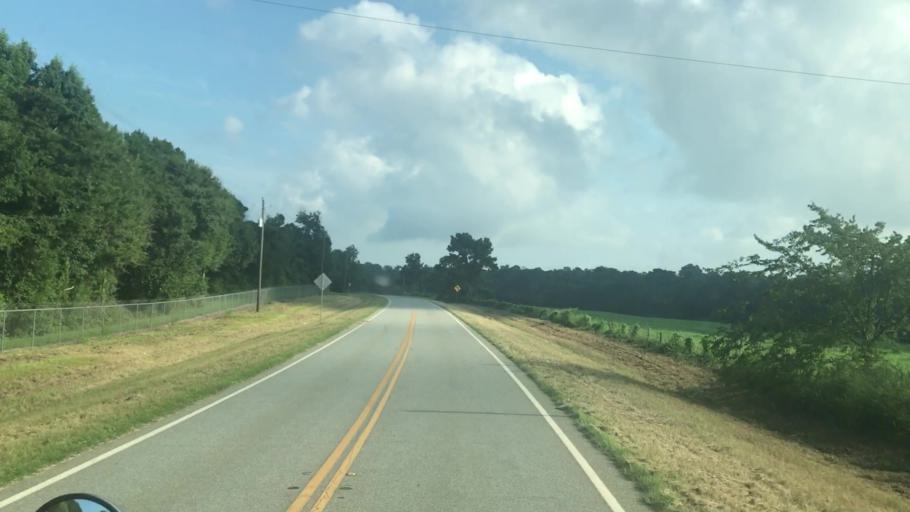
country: US
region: Florida
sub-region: Gadsden County
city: Havana
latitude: 30.7383
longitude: -84.4807
